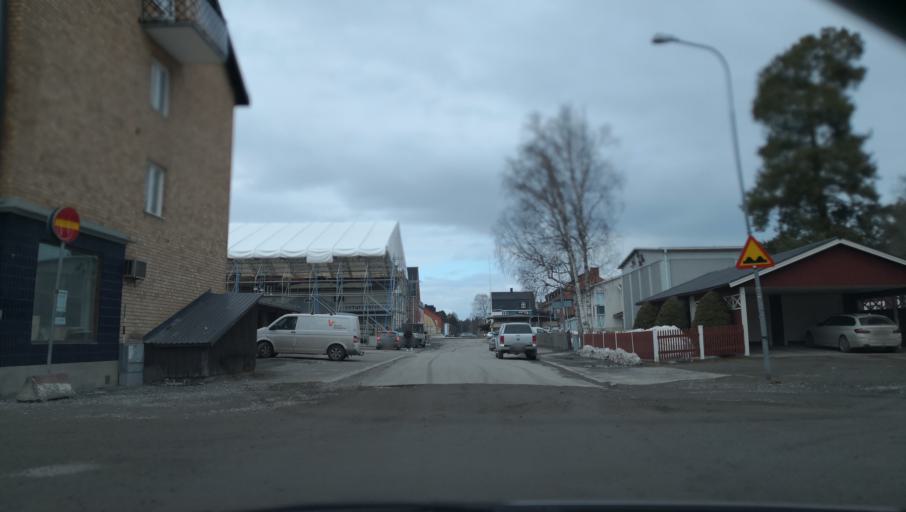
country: SE
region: Vaesterbotten
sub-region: Vannas Kommun
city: Vaennaes
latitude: 63.9074
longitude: 19.7535
